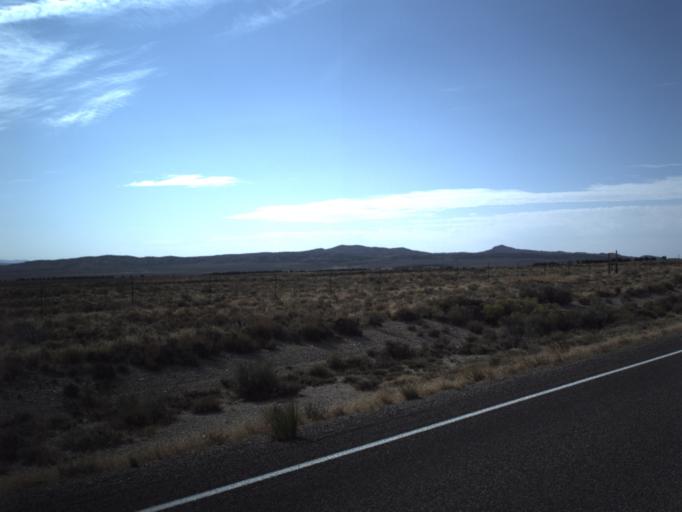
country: US
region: Idaho
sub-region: Cassia County
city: Burley
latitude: 41.7347
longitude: -113.5216
